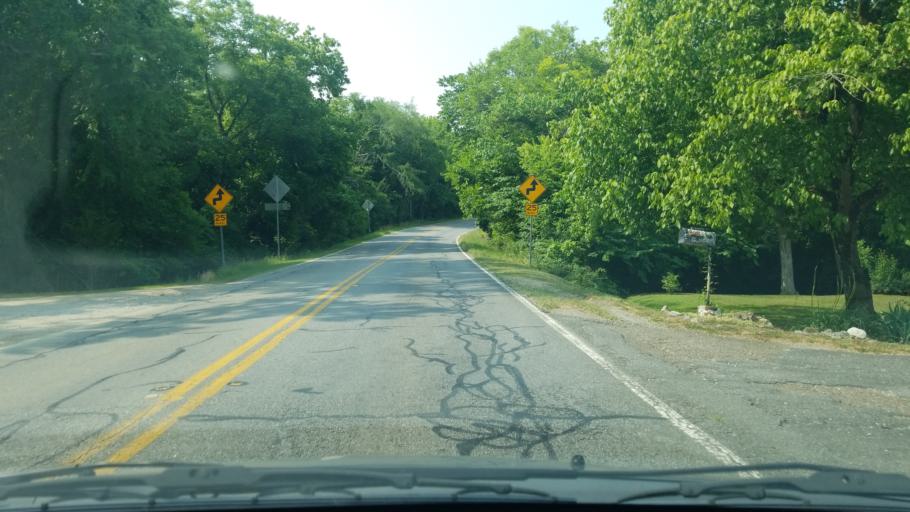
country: US
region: Georgia
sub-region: Catoosa County
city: Ringgold
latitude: 34.9201
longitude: -85.1044
